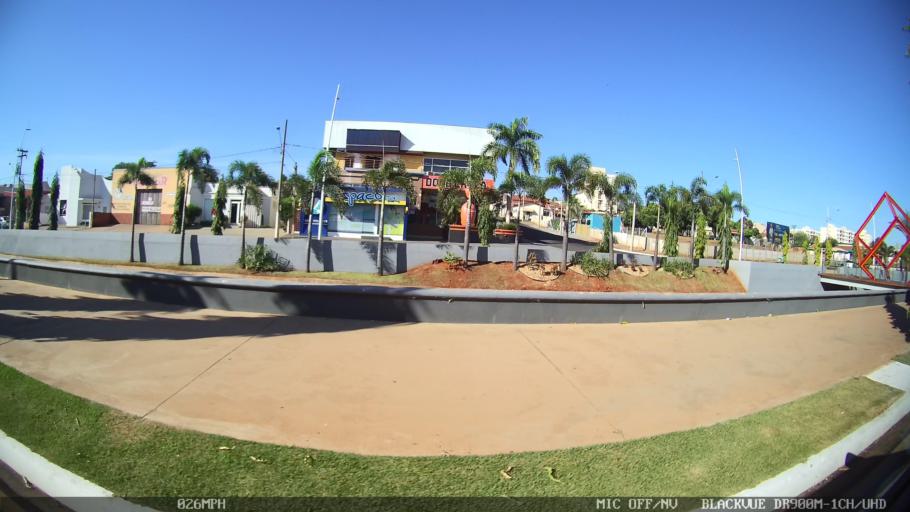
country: BR
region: Sao Paulo
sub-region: Olimpia
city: Olimpia
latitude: -20.7333
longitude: -48.9127
